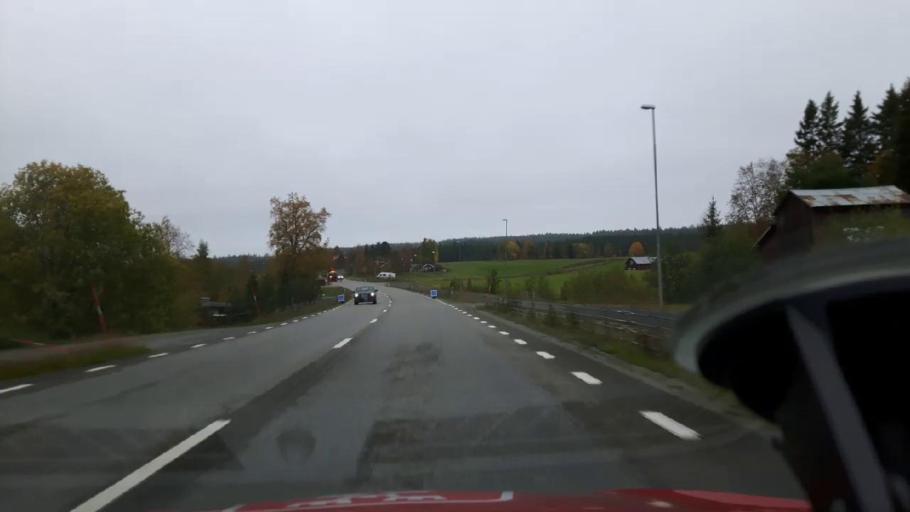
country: SE
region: Jaemtland
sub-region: Bergs Kommun
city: Hoverberg
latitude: 62.6887
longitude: 14.3975
